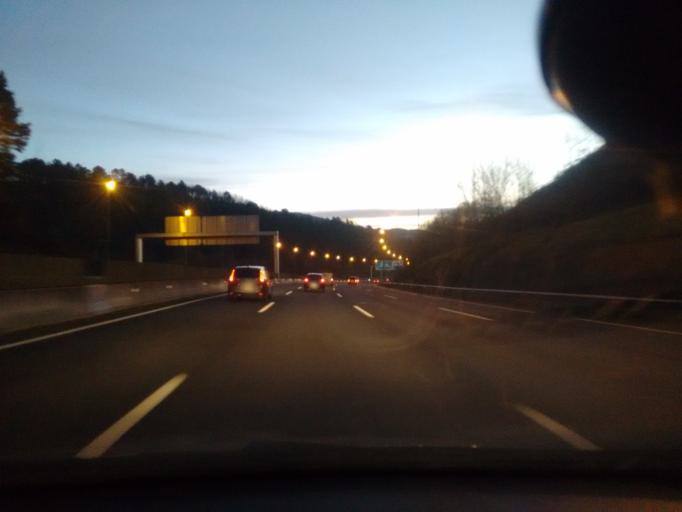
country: ES
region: Basque Country
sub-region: Bizkaia
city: Galdakao
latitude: 43.2358
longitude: -2.8535
